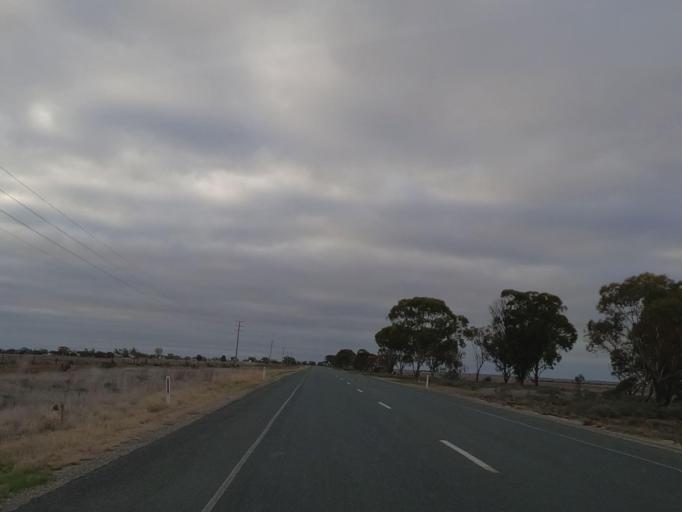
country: AU
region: Victoria
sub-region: Swan Hill
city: Swan Hill
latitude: -35.5902
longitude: 143.7904
